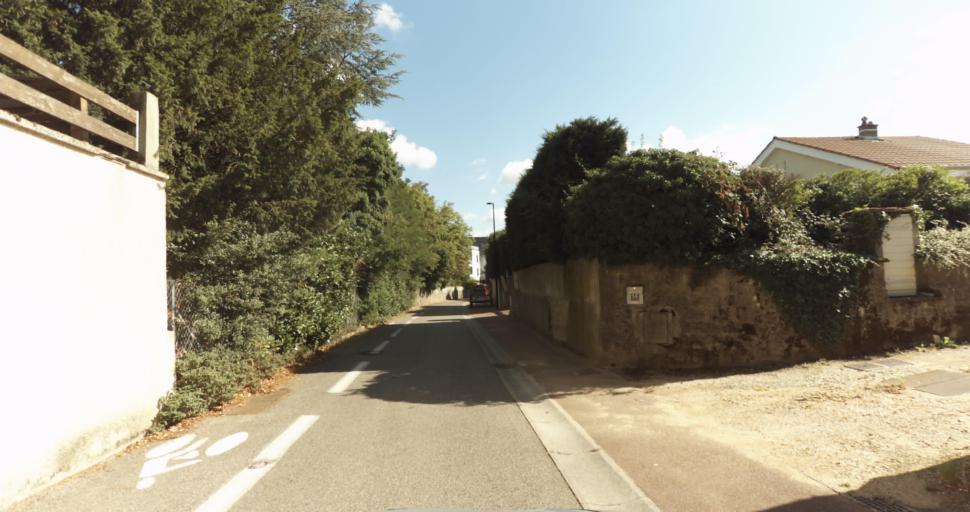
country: FR
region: Rhone-Alpes
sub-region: Departement du Rhone
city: Chaponost
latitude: 45.7137
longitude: 4.7446
